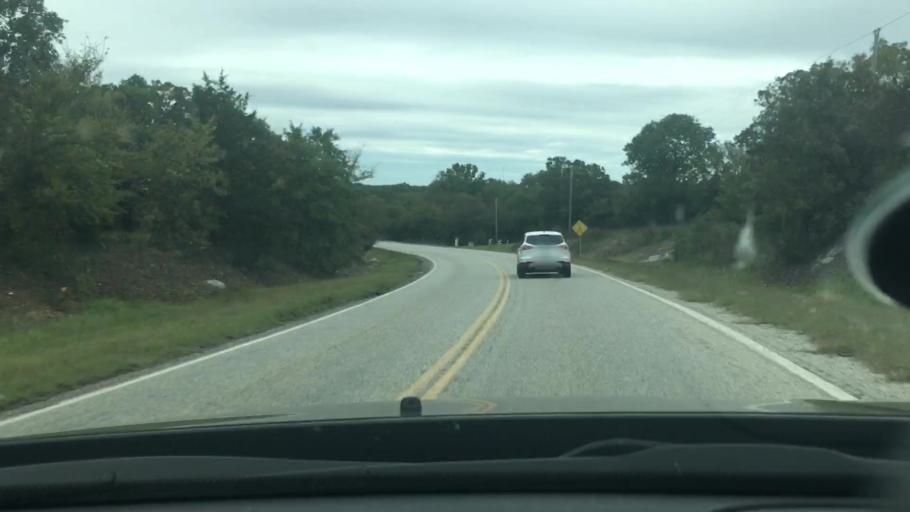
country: US
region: Oklahoma
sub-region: Johnston County
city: Tishomingo
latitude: 34.3268
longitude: -96.4199
